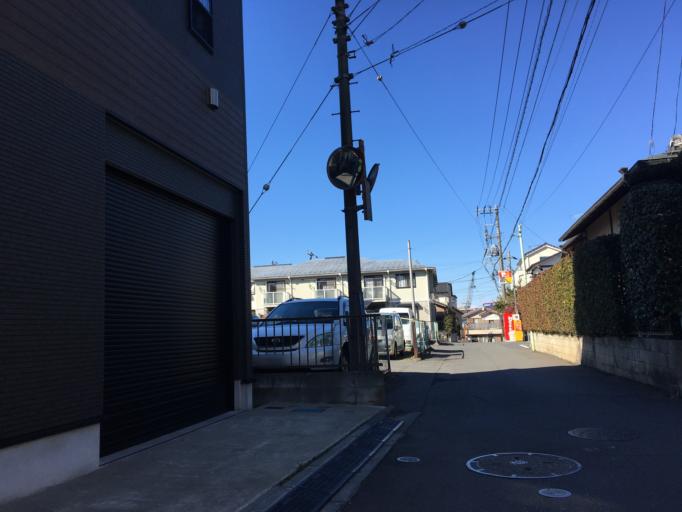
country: JP
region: Saitama
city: Oi
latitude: 35.8382
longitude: 139.5391
